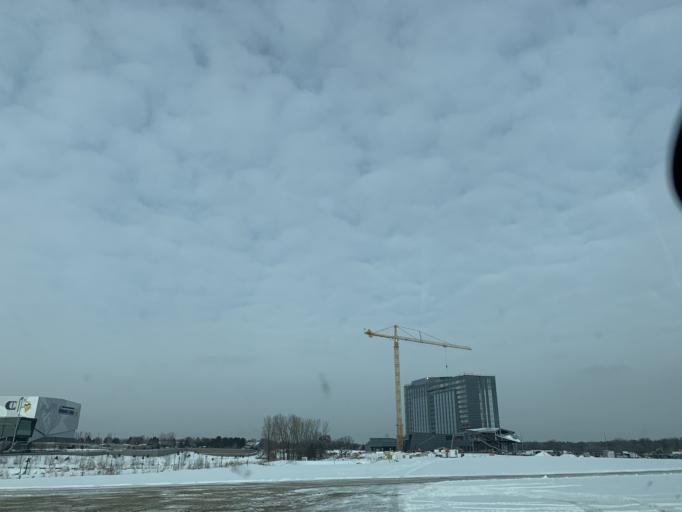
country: US
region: Minnesota
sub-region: Dakota County
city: Mendota Heights
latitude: 44.8572
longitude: -93.1132
